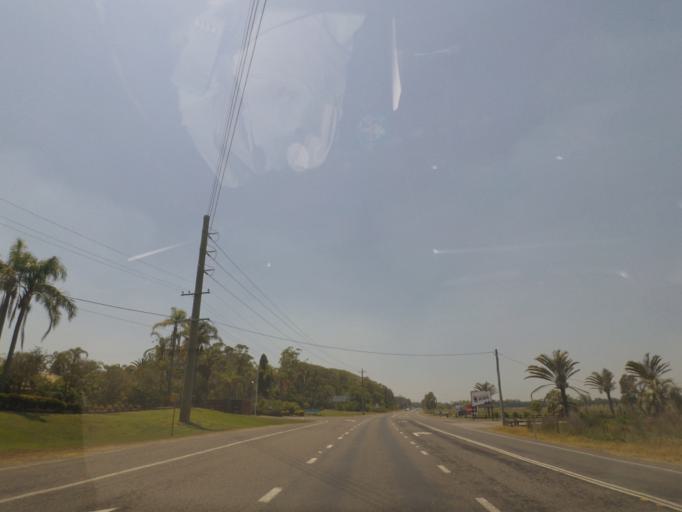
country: AU
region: New South Wales
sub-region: Port Stephens Shire
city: Medowie
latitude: -32.8068
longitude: 151.8625
